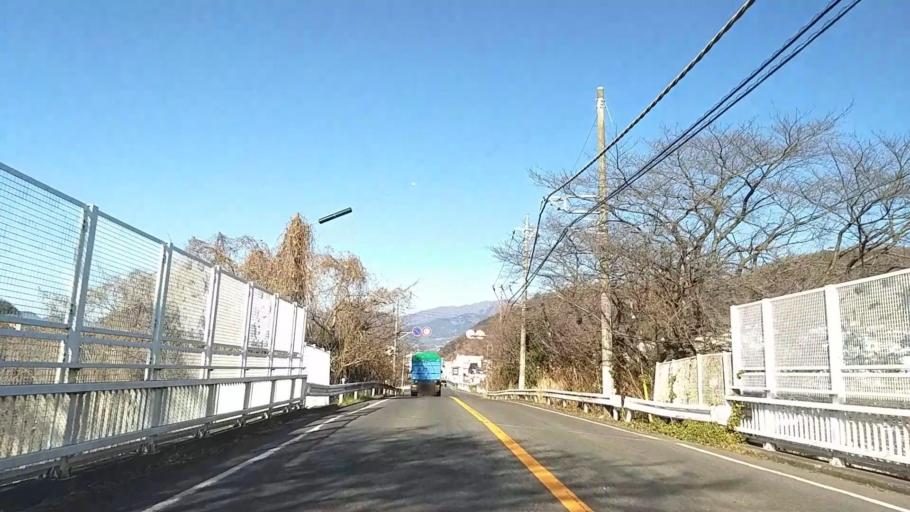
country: JP
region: Kanagawa
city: Hadano
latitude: 35.3632
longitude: 139.2465
